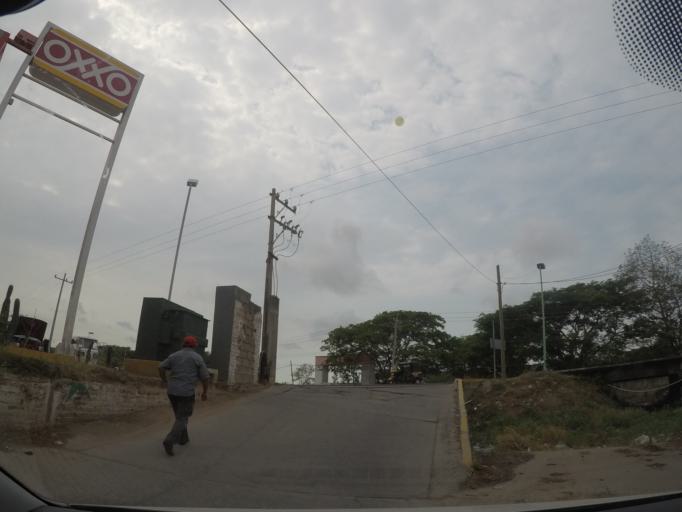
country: MX
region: Oaxaca
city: Juchitan de Zaragoza
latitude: 16.4478
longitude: -95.0148
